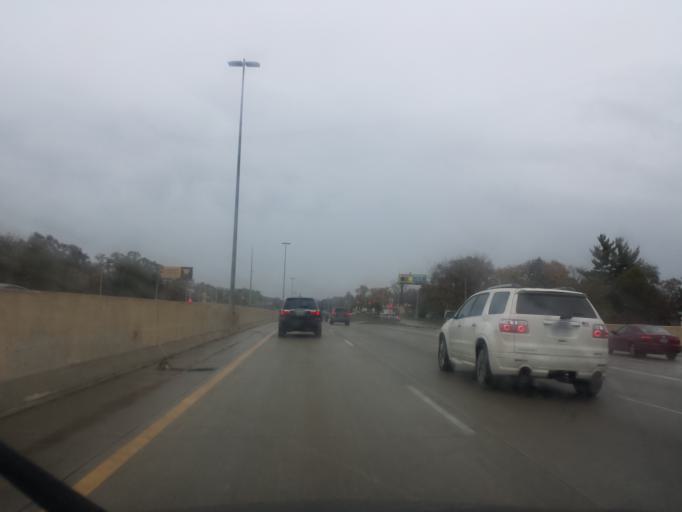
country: US
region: Michigan
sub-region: Oakland County
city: Southfield
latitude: 42.4272
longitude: -83.2192
